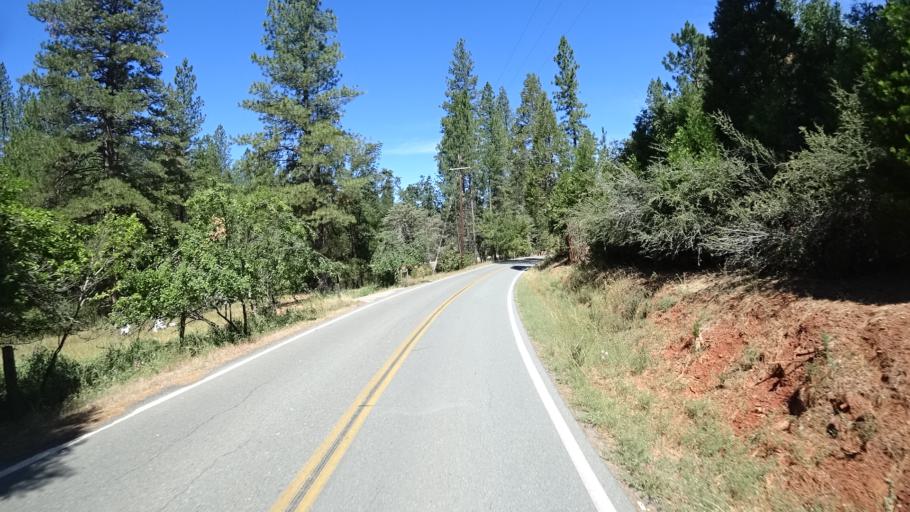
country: US
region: California
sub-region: Amador County
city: Pioneer
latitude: 38.3508
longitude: -120.5201
